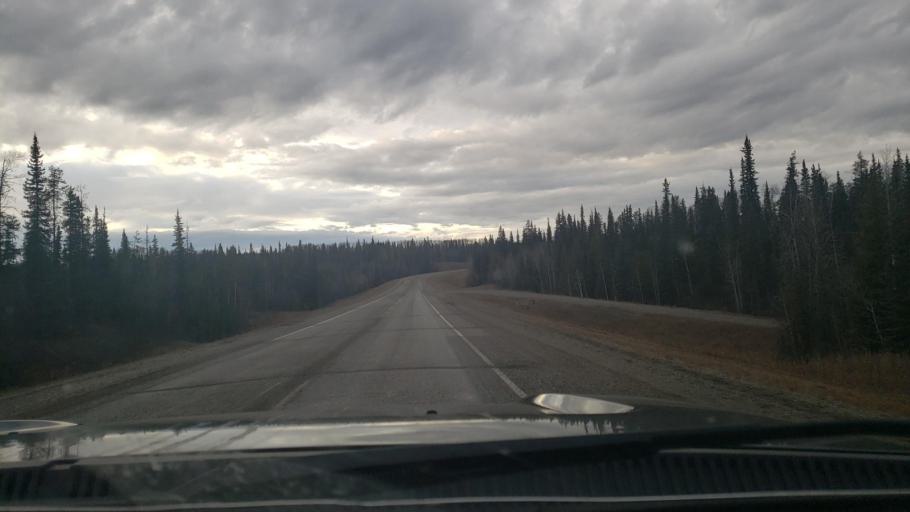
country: CA
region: Yukon
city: Watson Lake
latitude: 59.9828
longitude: -127.5861
